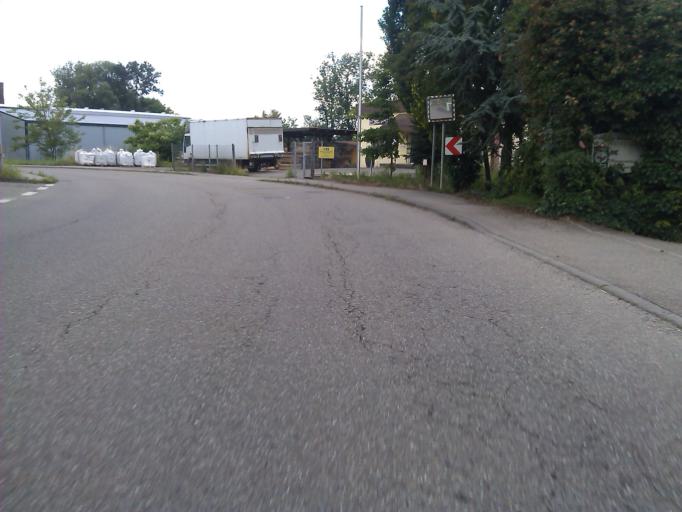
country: DE
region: Baden-Wuerttemberg
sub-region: Regierungsbezirk Stuttgart
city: Bonnigheim
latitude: 49.0739
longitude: 9.1050
